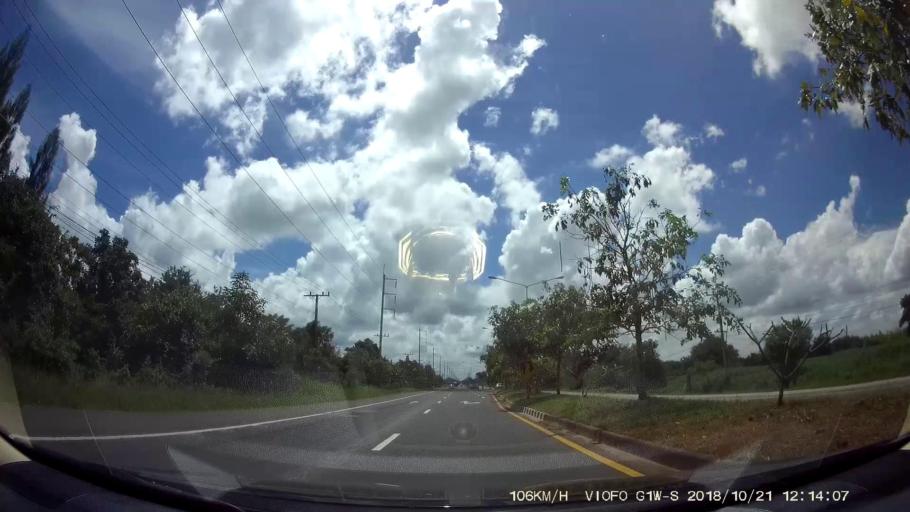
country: TH
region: Chaiyaphum
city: Chatturat
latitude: 15.3825
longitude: 101.8367
